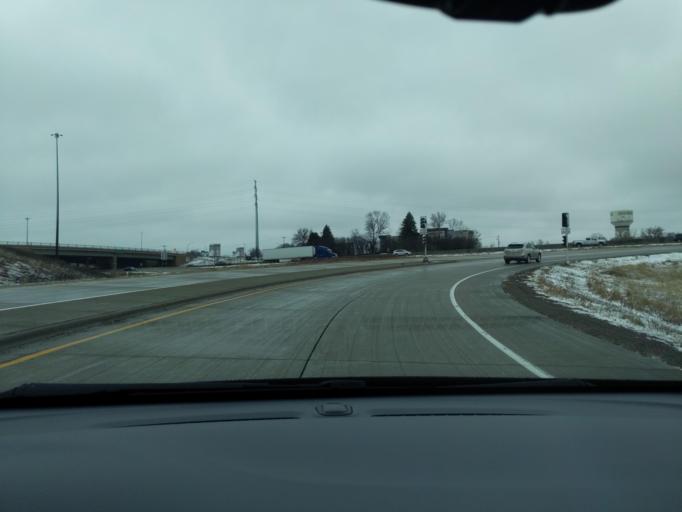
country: US
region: Minnesota
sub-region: Hennepin County
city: Eden Prairie
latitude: 44.8644
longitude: -93.4263
